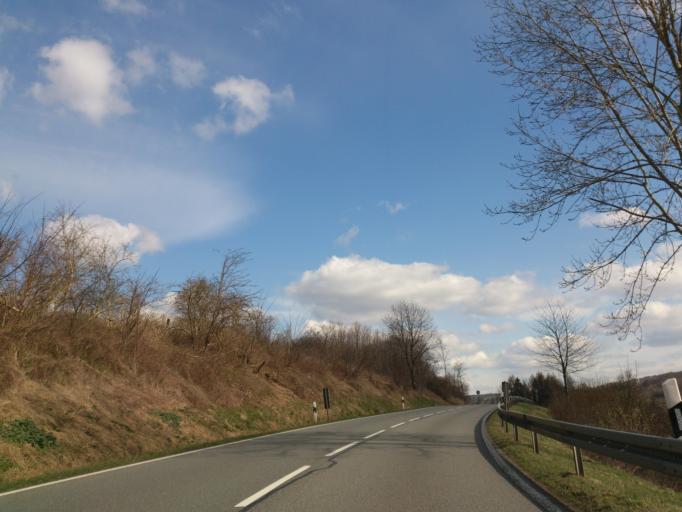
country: DE
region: North Rhine-Westphalia
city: Brakel
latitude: 51.7132
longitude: 9.2805
